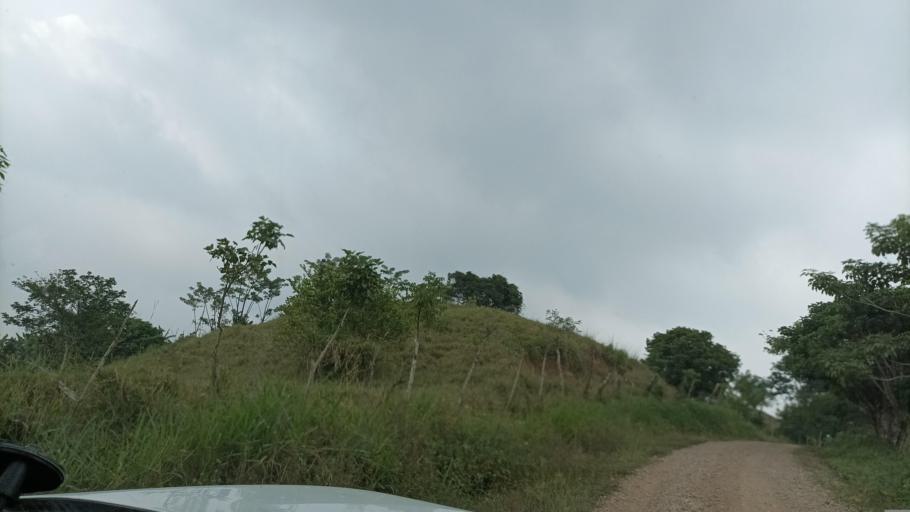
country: MX
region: Veracruz
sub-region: Uxpanapa
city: Poblado 10
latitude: 17.5712
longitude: -94.2280
